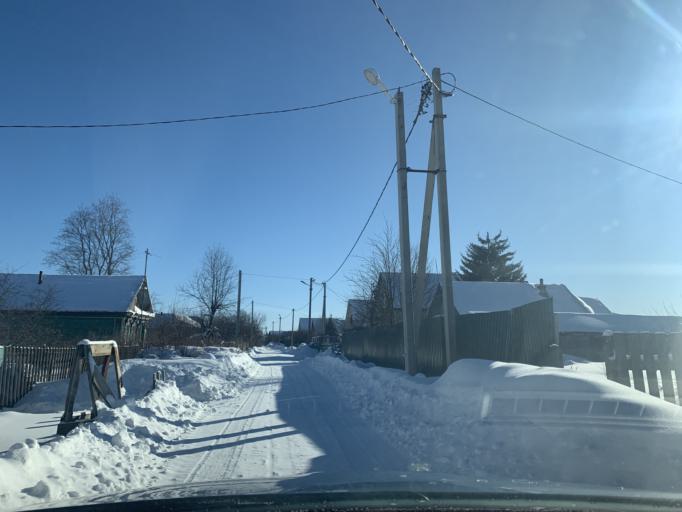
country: RU
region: Jaroslavl
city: Tunoshna
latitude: 57.6527
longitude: 40.0609
